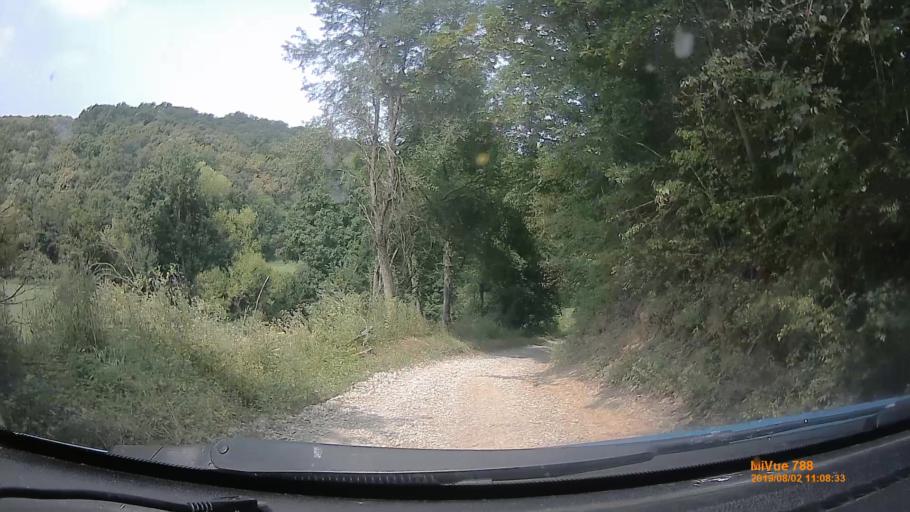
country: HU
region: Baranya
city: Buekkoesd
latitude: 46.1005
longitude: 17.9434
